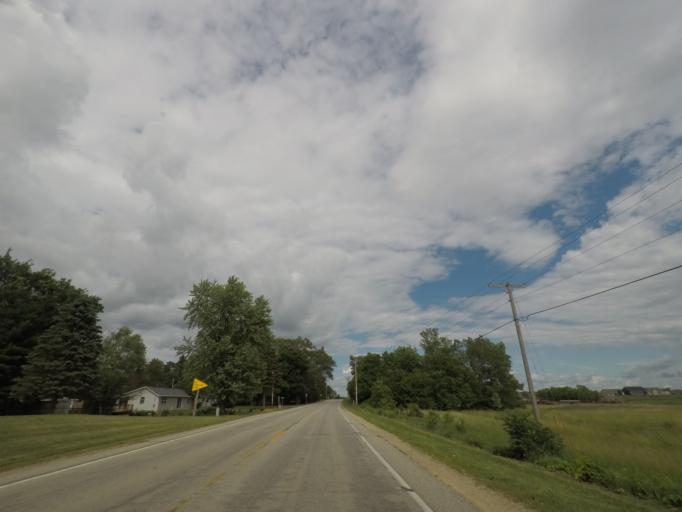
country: US
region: Wisconsin
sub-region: Dane County
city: Belleville
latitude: 42.8281
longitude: -89.5045
